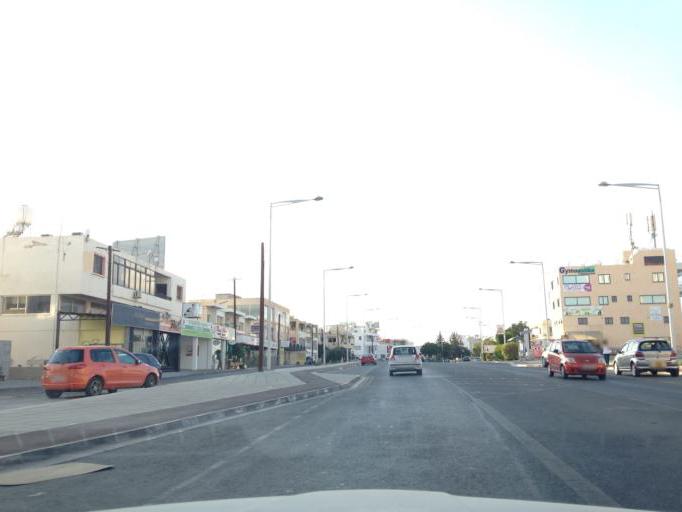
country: CY
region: Pafos
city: Paphos
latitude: 34.7638
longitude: 32.4482
